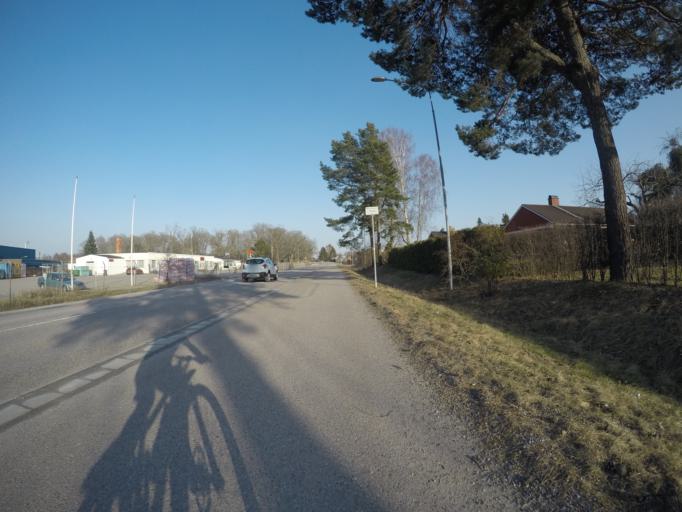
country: SE
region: Vaestmanland
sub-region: Kungsors Kommun
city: Kungsoer
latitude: 59.4267
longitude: 16.1091
